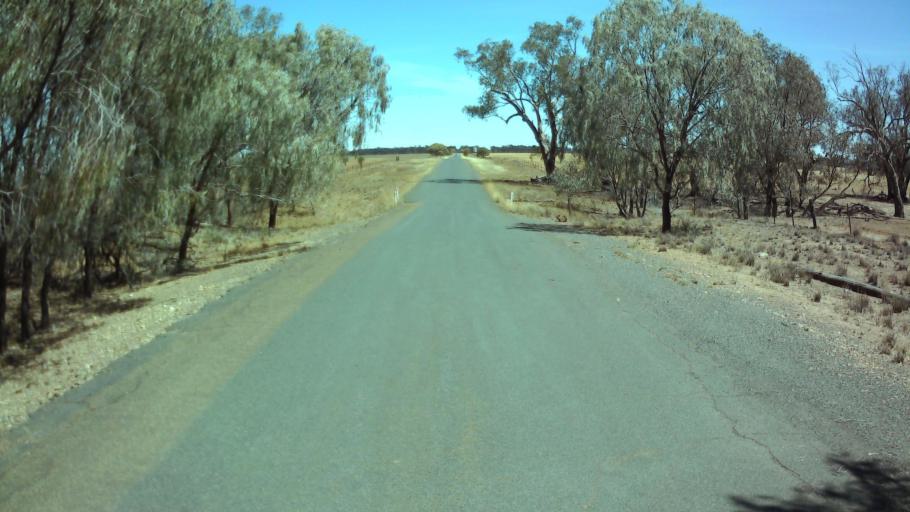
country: AU
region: New South Wales
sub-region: Weddin
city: Grenfell
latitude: -33.8491
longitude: 147.6959
